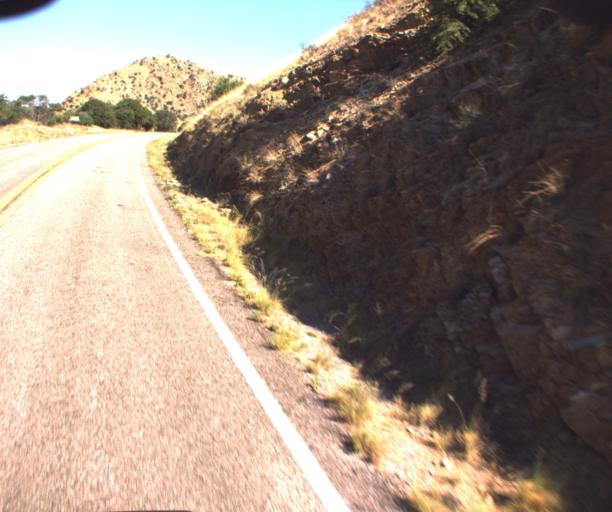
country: US
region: Arizona
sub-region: Graham County
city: Swift Trail Junction
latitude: 32.5779
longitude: -109.8485
